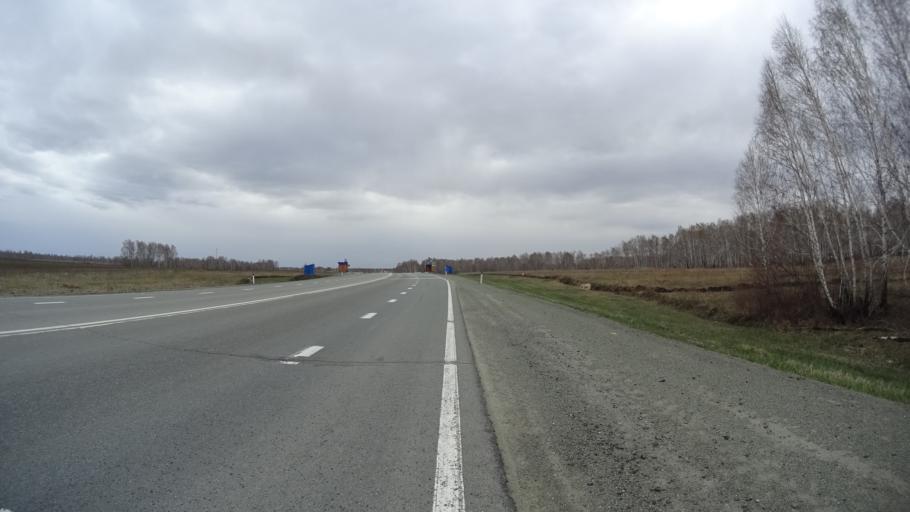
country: RU
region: Chelyabinsk
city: Yemanzhelinsk
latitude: 54.6974
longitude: 61.2502
